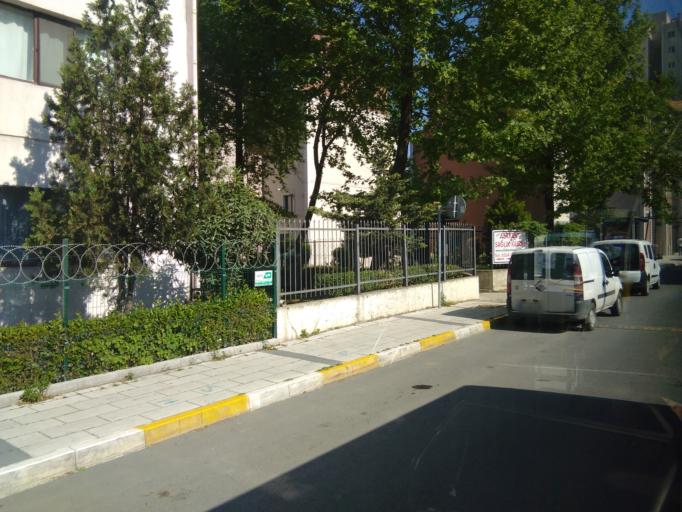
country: TR
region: Istanbul
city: Mahmutbey
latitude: 41.0478
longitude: 28.7978
